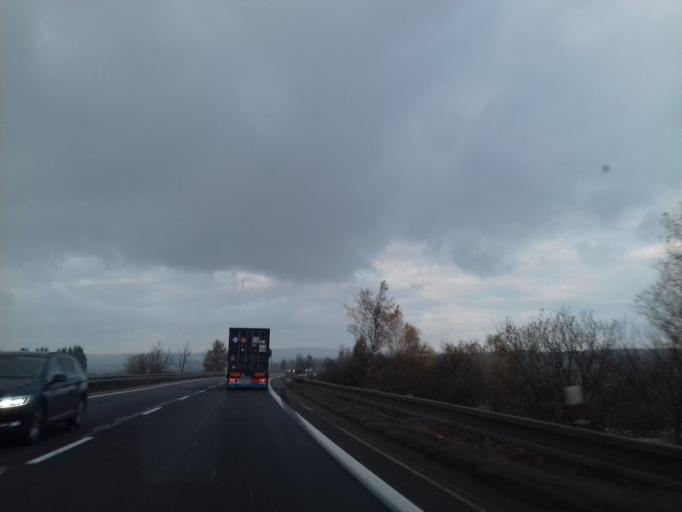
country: CZ
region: Pardubicky
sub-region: Okres Svitavy
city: Svitavy
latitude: 49.7586
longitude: 16.5404
